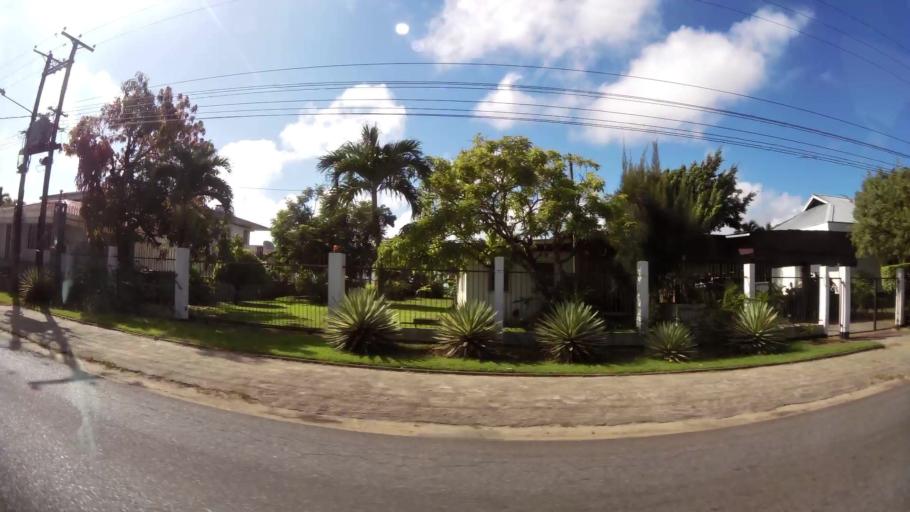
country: SR
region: Paramaribo
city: Paramaribo
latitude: 5.8381
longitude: -55.1216
